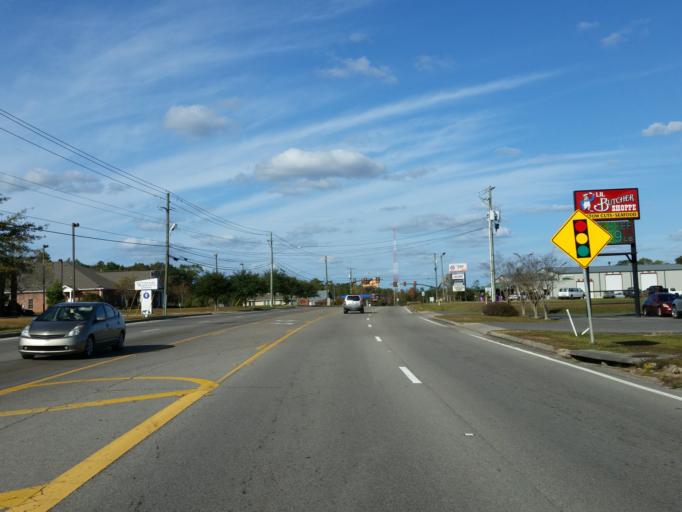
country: US
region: Mississippi
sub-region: Forrest County
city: Hattiesburg
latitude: 31.2974
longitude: -89.3242
